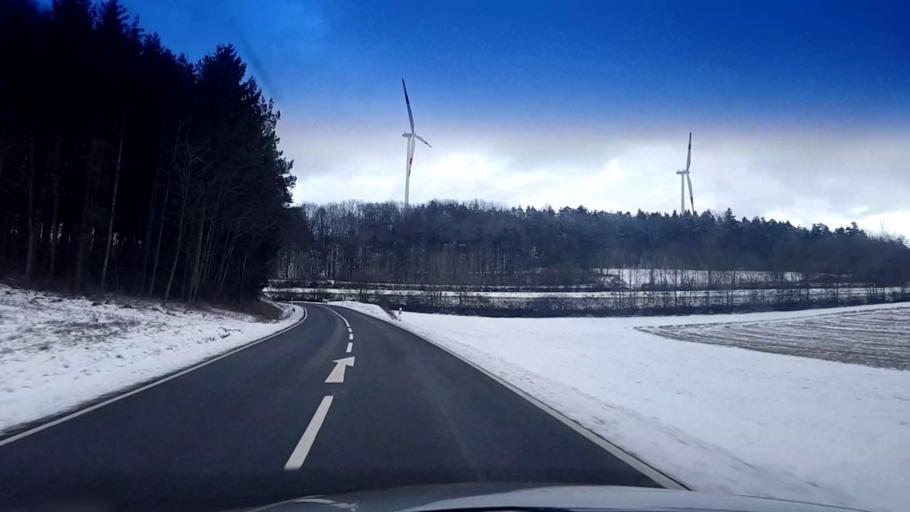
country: DE
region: Bavaria
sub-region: Upper Franconia
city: Buttenheim
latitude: 49.8530
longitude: 11.0859
